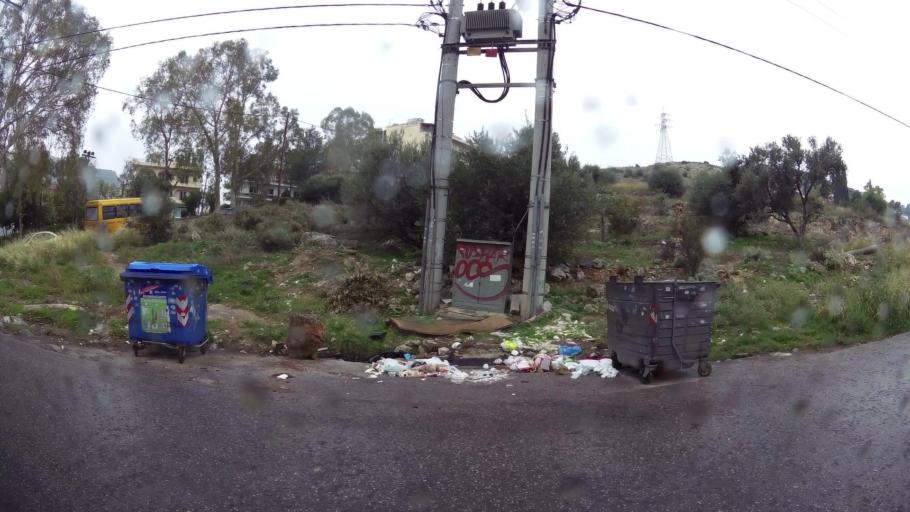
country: GR
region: Attica
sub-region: Nomos Piraios
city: Korydallos
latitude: 38.0002
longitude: 23.6429
